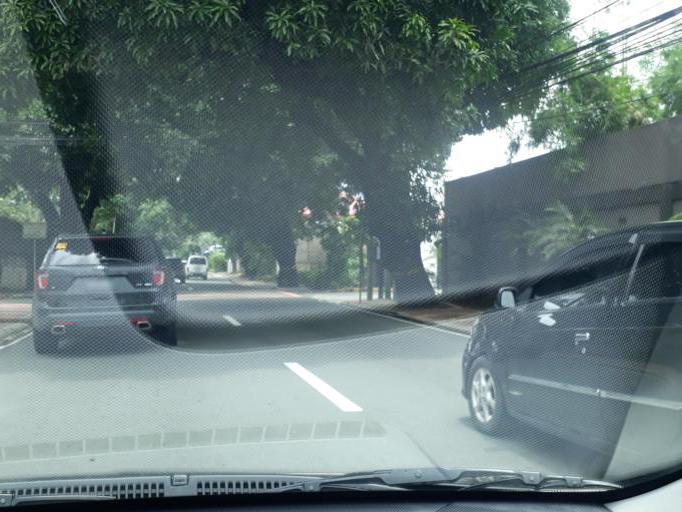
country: PH
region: Metro Manila
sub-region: San Juan
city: San Juan
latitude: 14.6165
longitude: 121.0330
